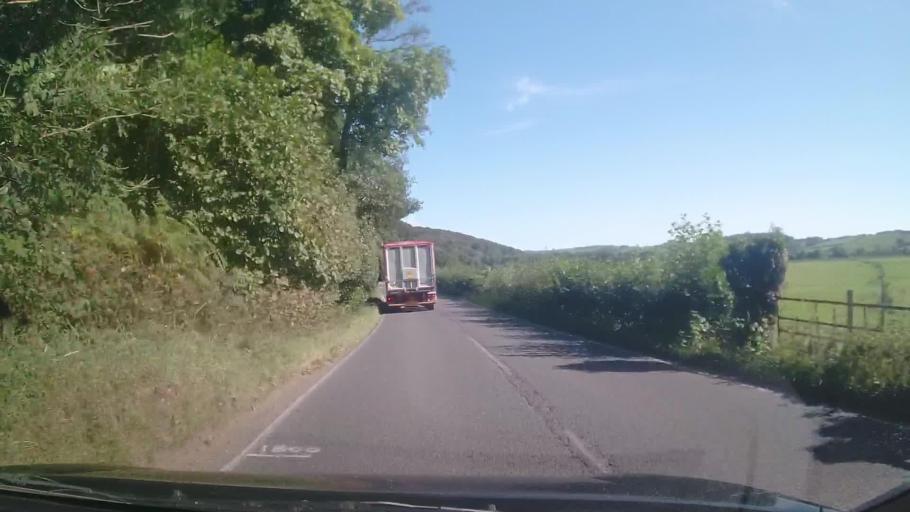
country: GB
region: England
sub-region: Cumbria
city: Millom
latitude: 54.2800
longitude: -3.2348
